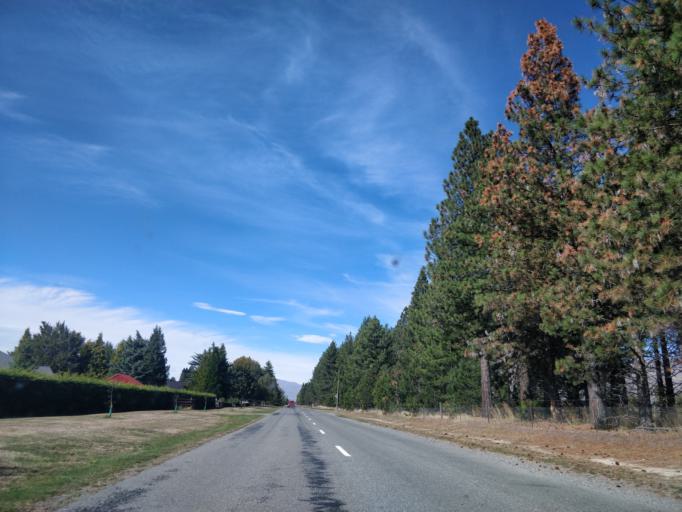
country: NZ
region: Canterbury
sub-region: Timaru District
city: Pleasant Point
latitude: -44.2465
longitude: 170.0946
